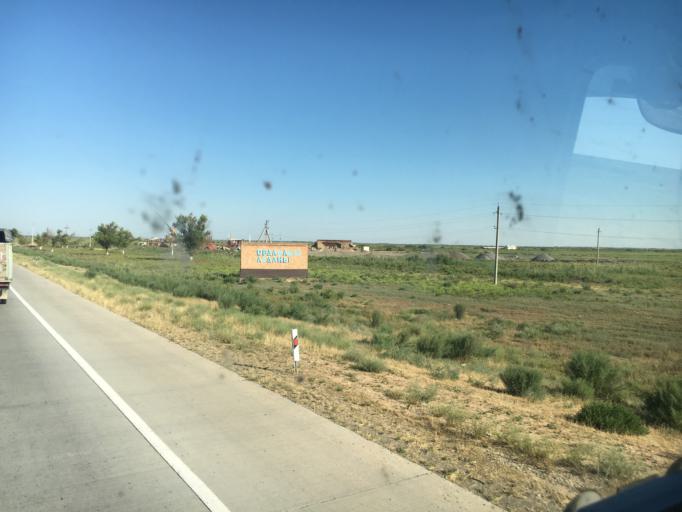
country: KZ
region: Ongtustik Qazaqstan
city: Bayaldyr
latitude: 42.9949
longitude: 68.8059
